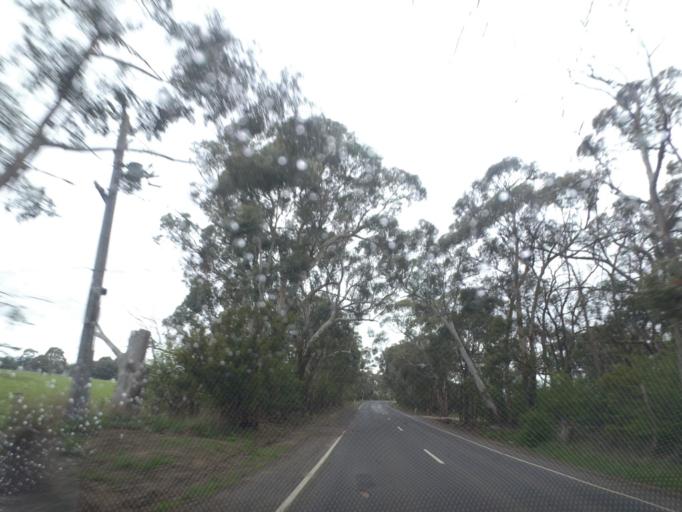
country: AU
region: Victoria
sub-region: Hume
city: Sunbury
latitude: -37.3443
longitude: 144.6896
